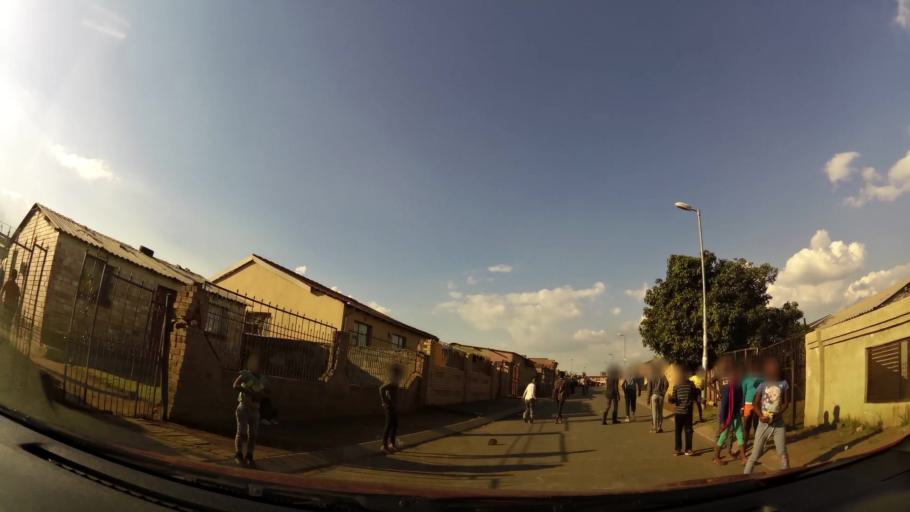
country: ZA
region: Gauteng
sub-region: City of Johannesburg Metropolitan Municipality
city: Soweto
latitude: -26.2384
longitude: 27.8541
